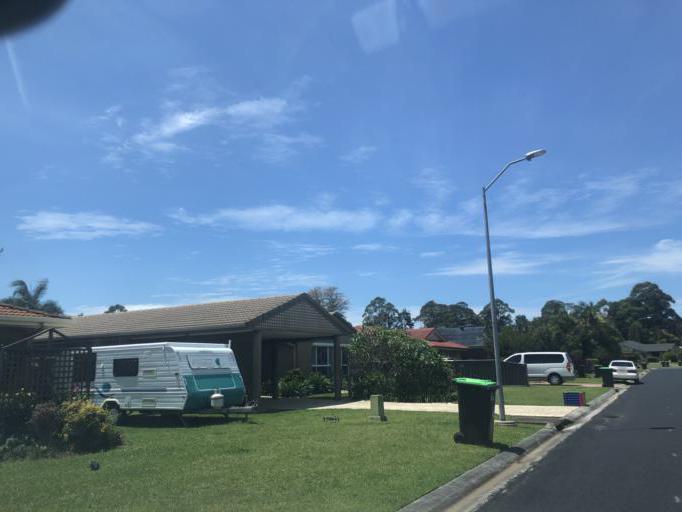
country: AU
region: New South Wales
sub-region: Coffs Harbour
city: Coffs Harbour
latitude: -30.2879
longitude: 153.0942
